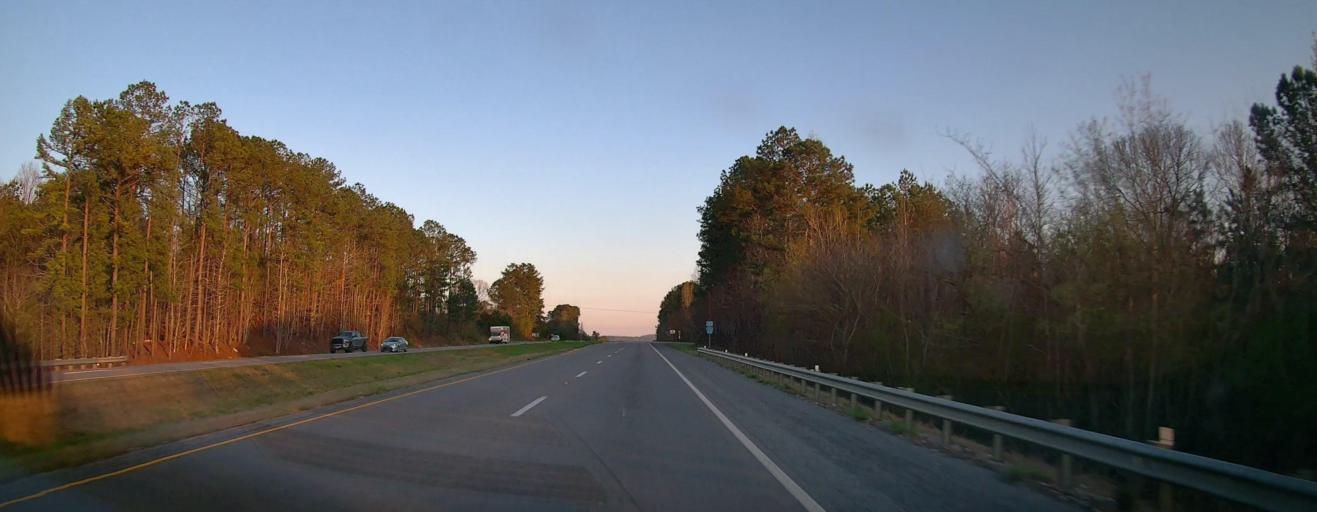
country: US
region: Alabama
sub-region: Coosa County
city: Stewartville
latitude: 33.1093
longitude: -86.2323
